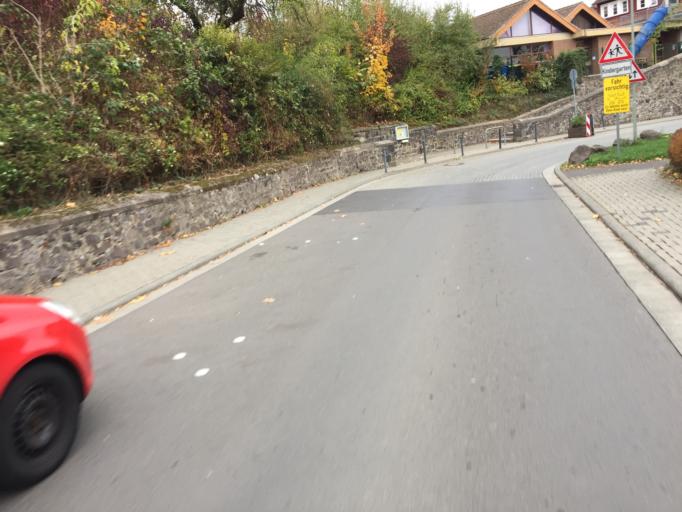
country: DE
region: Hesse
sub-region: Regierungsbezirk Giessen
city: Lich
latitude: 50.5212
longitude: 8.8220
